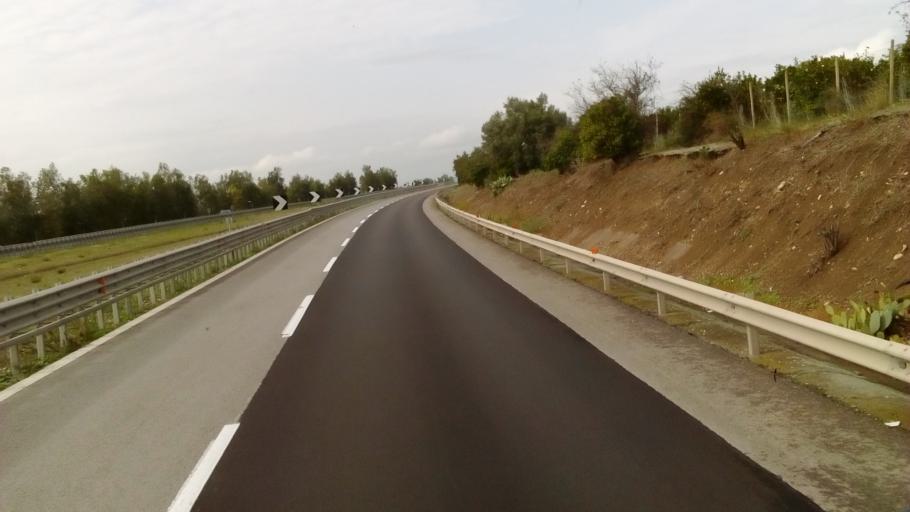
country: IT
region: Sicily
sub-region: Catania
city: Paterno
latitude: 37.4680
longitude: 14.8718
